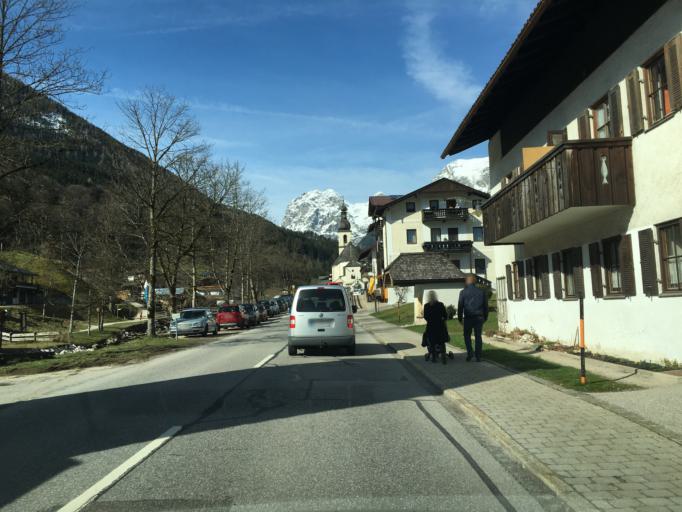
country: DE
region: Bavaria
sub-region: Upper Bavaria
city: Ramsau
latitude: 47.6078
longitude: 12.8980
